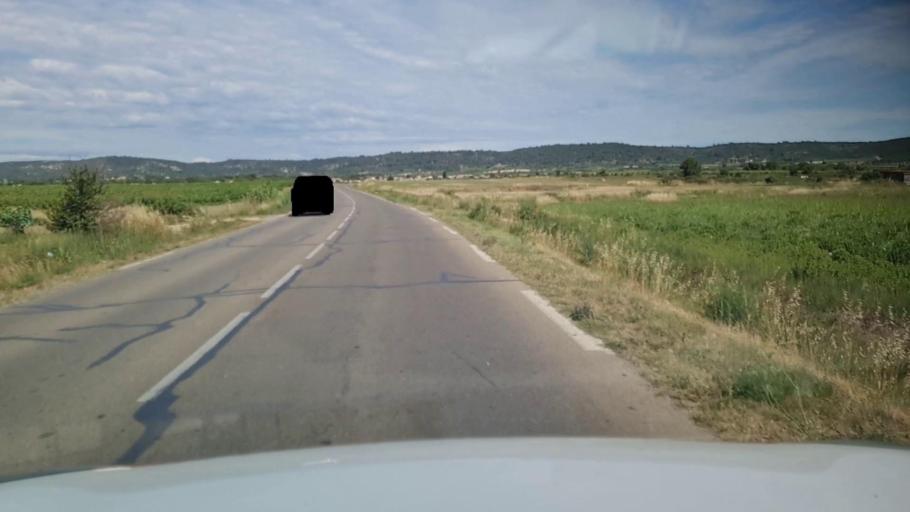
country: FR
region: Languedoc-Roussillon
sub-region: Departement du Gard
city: Langlade
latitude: 43.8131
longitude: 4.2427
